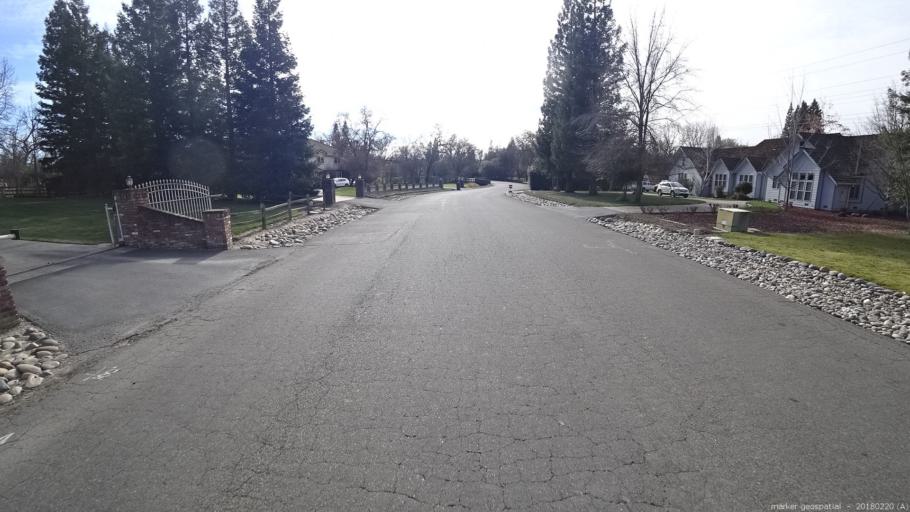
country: US
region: California
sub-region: Sacramento County
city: Orangevale
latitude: 38.7101
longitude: -121.2359
